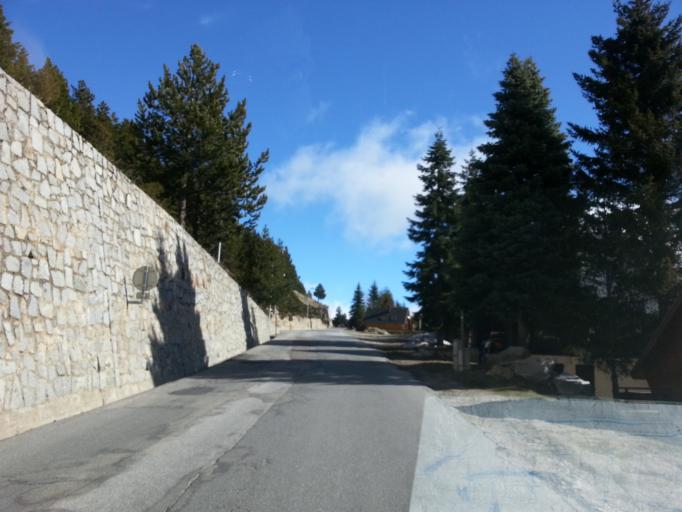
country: ES
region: Catalonia
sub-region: Provincia de Girona
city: Llivia
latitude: 42.5856
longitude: 2.0747
